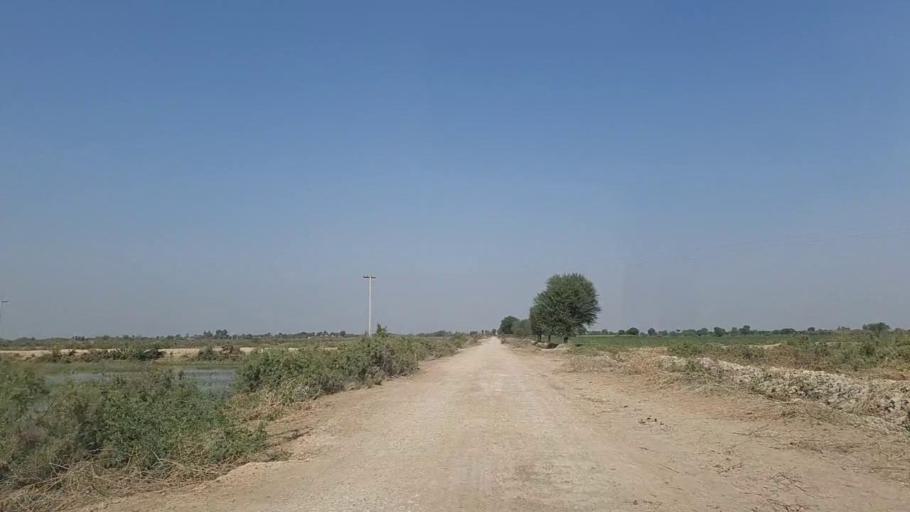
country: PK
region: Sindh
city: Samaro
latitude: 25.2069
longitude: 69.4042
